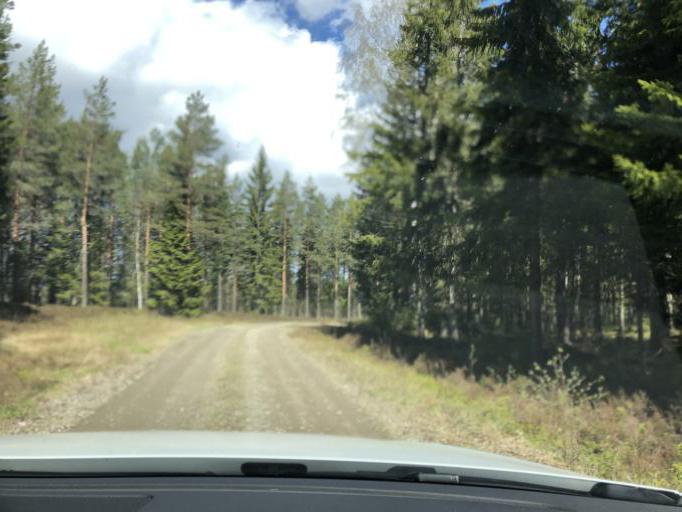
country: SE
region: Dalarna
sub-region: Avesta Kommun
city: Horndal
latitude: 60.2283
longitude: 16.5934
